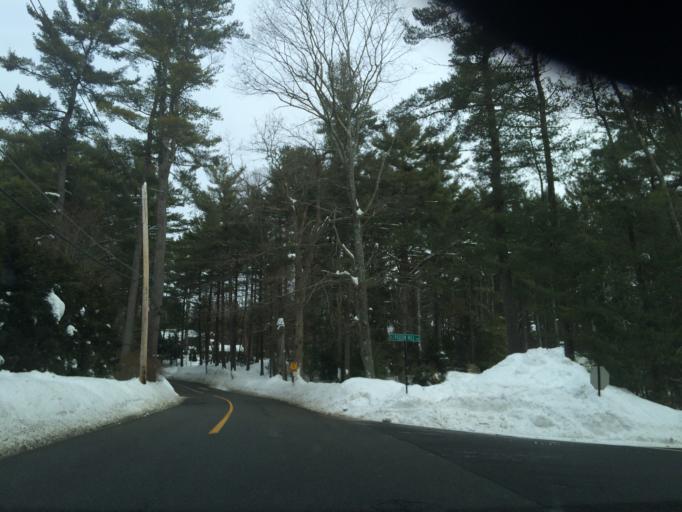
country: US
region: Massachusetts
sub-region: Middlesex County
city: Weston
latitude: 42.3753
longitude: -71.2999
